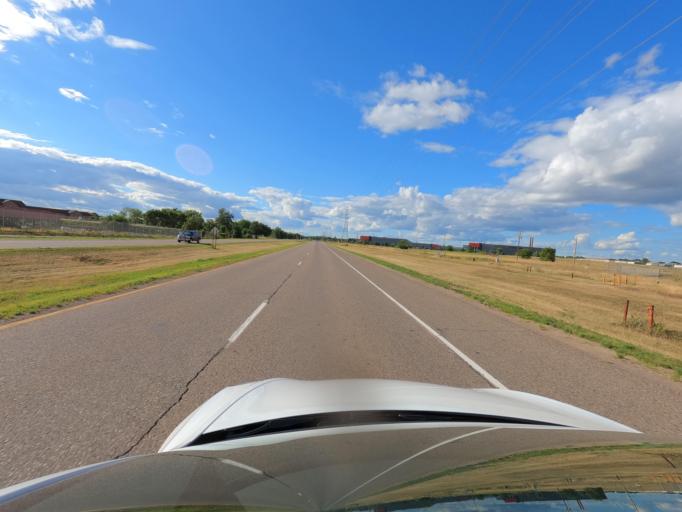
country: US
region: Minnesota
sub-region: Anoka County
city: Columbia Heights
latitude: 45.0492
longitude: -93.2755
